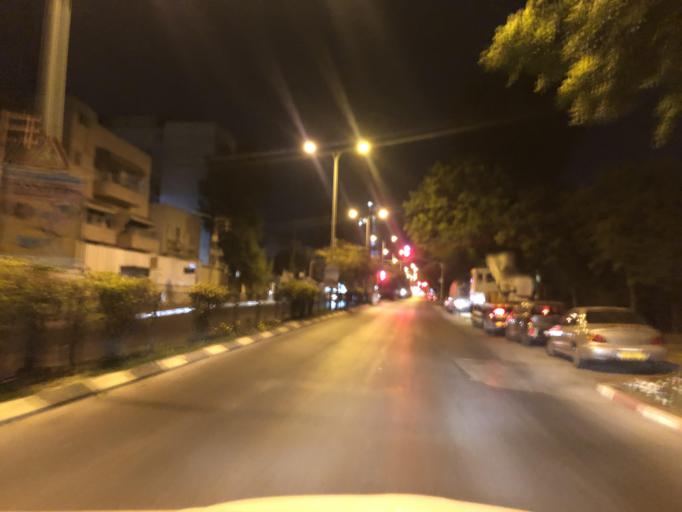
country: IL
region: Tel Aviv
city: Azor
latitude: 32.0475
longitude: 34.7955
